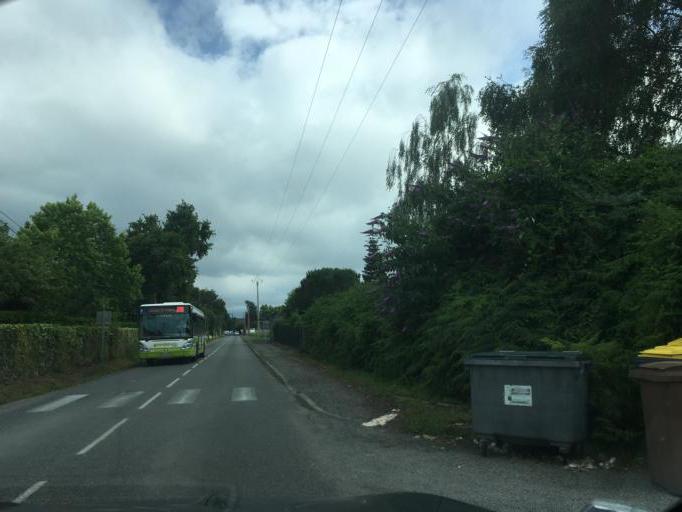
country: FR
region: Aquitaine
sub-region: Departement des Pyrenees-Atlantiques
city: Ousse
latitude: 43.2929
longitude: -0.2720
